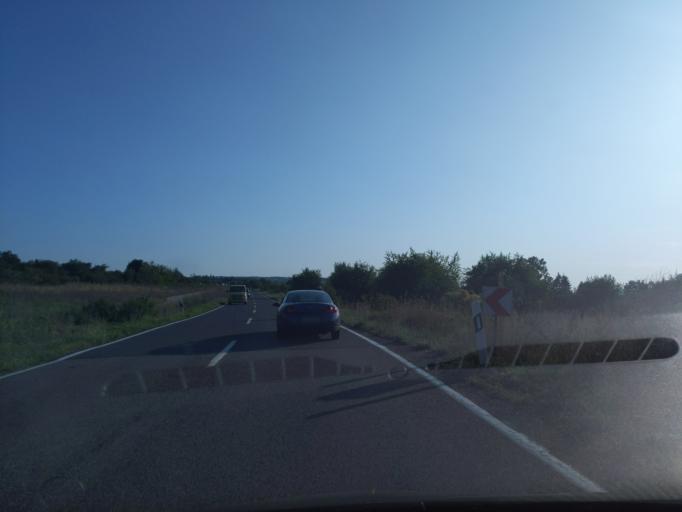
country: DE
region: Rheinland-Pfalz
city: Nieder-Ingelheim
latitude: 49.9914
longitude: 8.0796
